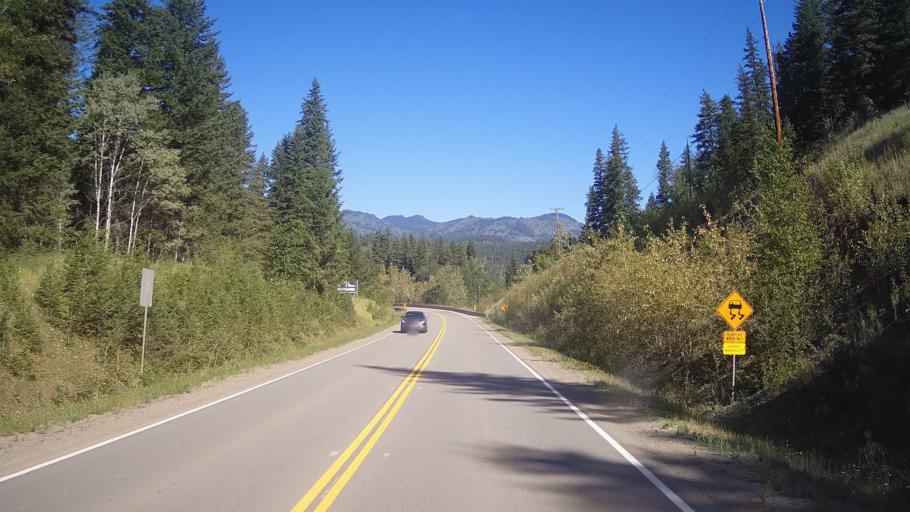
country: CA
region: British Columbia
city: Kamloops
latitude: 51.4517
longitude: -120.2149
